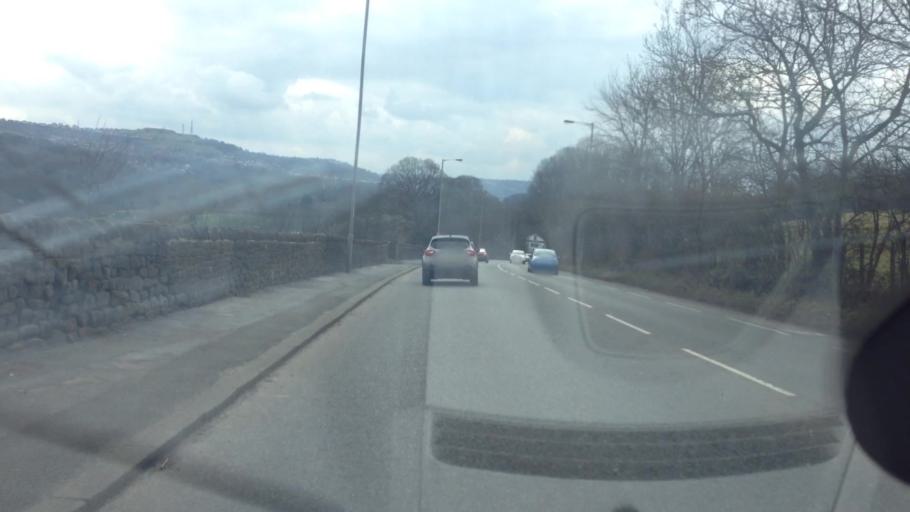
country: GB
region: England
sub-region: City and Borough of Leeds
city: Guiseley
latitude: 53.8583
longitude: -1.7372
